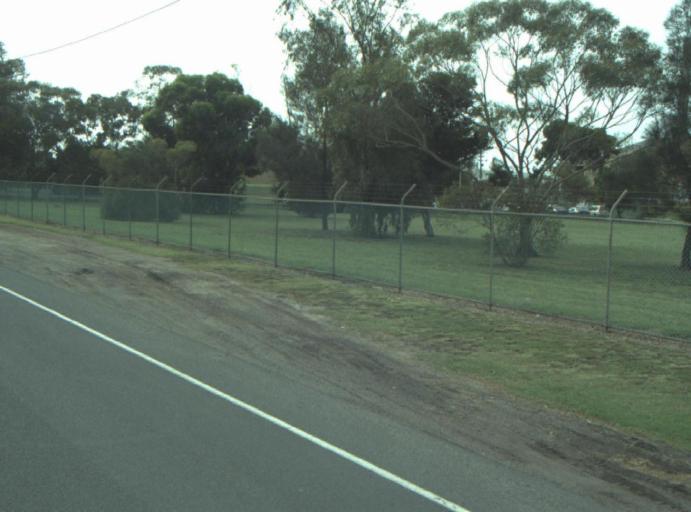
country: AU
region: Victoria
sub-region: Greater Geelong
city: Bell Park
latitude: -38.0858
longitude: 144.3796
